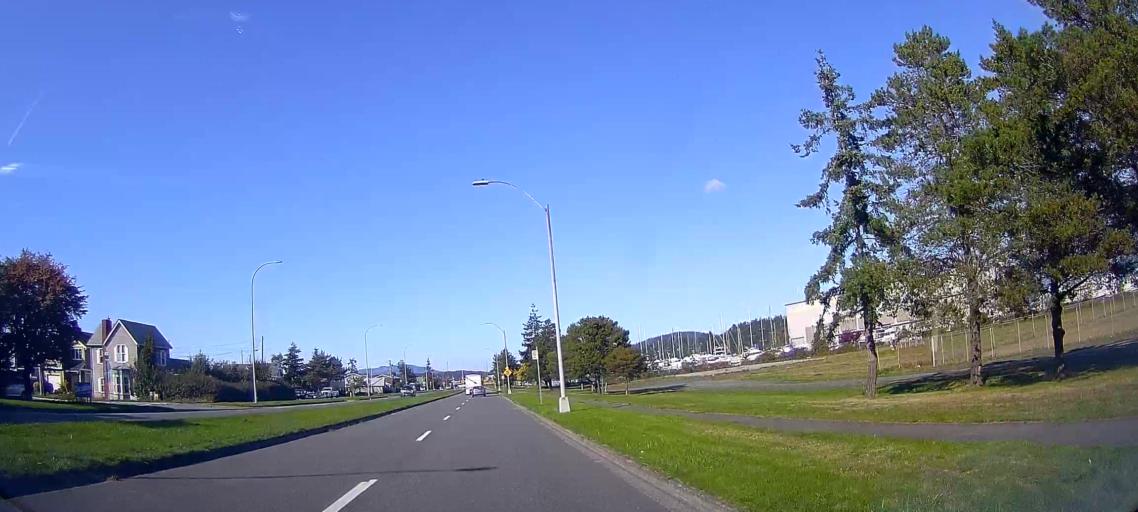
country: US
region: Washington
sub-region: Skagit County
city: Anacortes
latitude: 48.5017
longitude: -122.6095
